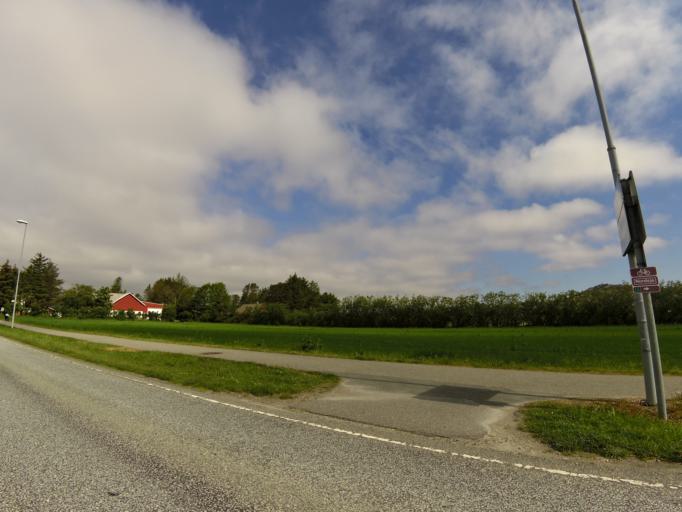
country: NO
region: Rogaland
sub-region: Ha
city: Vigrestad
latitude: 58.5216
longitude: 5.7997
